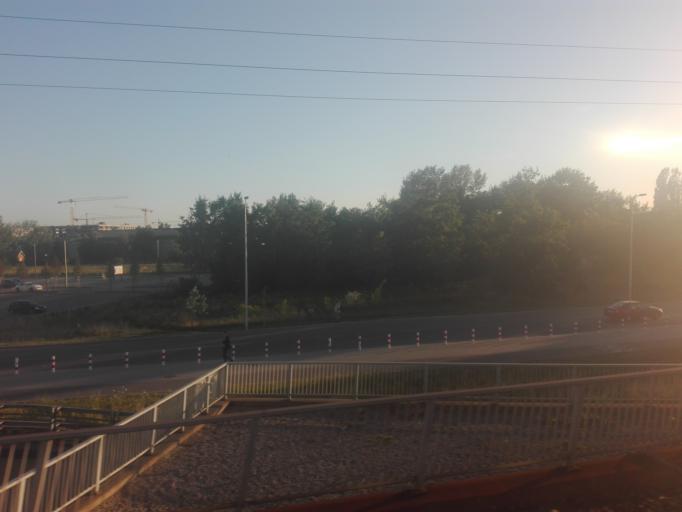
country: PL
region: Masovian Voivodeship
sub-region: Warszawa
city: Ursus
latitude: 52.2046
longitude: 20.8924
